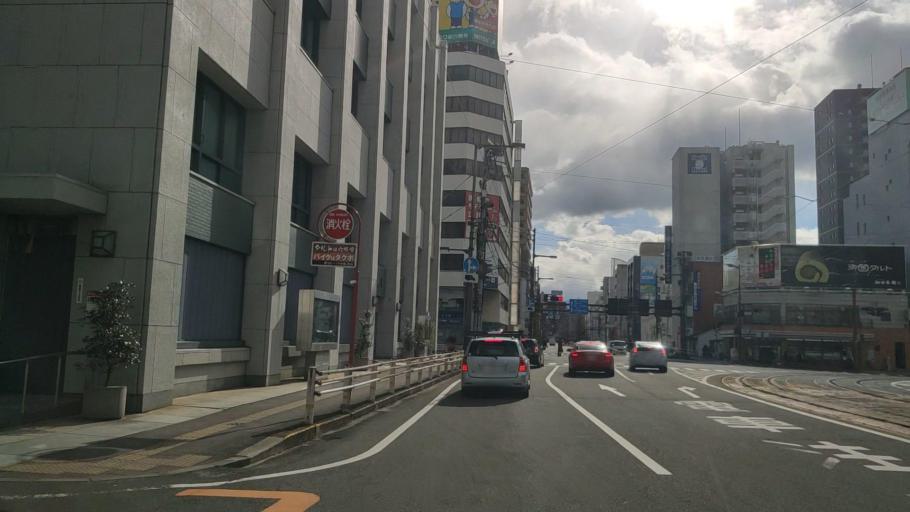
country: JP
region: Ehime
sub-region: Shikoku-chuo Shi
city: Matsuyama
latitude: 33.8422
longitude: 132.7755
